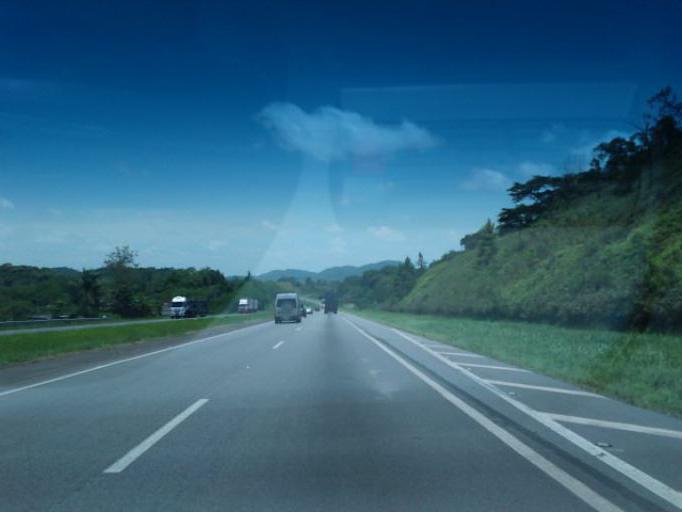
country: BR
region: Sao Paulo
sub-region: Juquia
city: Juquia
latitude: -24.3307
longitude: -47.6133
